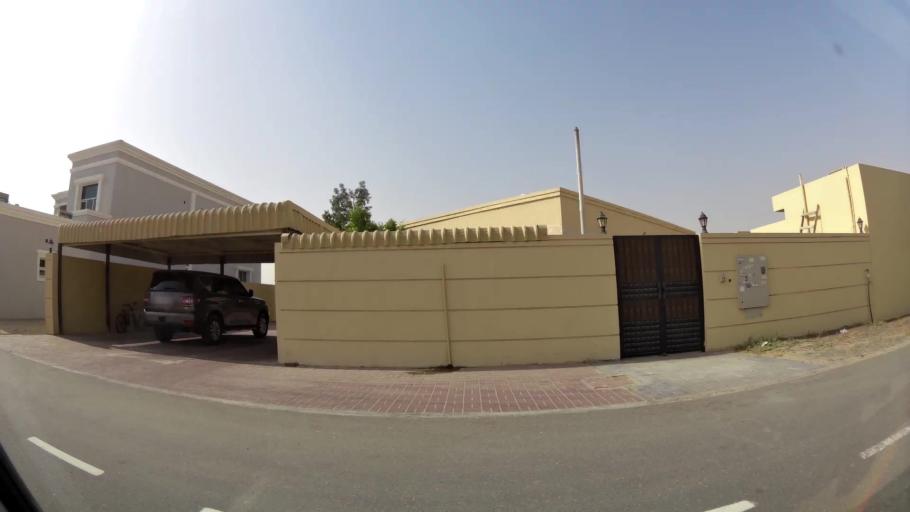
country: AE
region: Ash Shariqah
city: Sharjah
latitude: 25.2571
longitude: 55.4527
